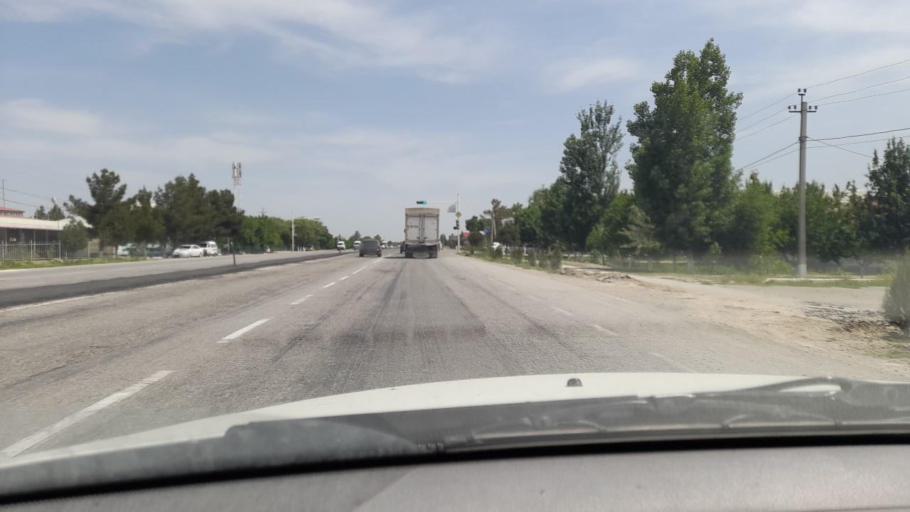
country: UZ
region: Navoiy
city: Beshrabot
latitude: 40.1363
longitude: 65.2574
